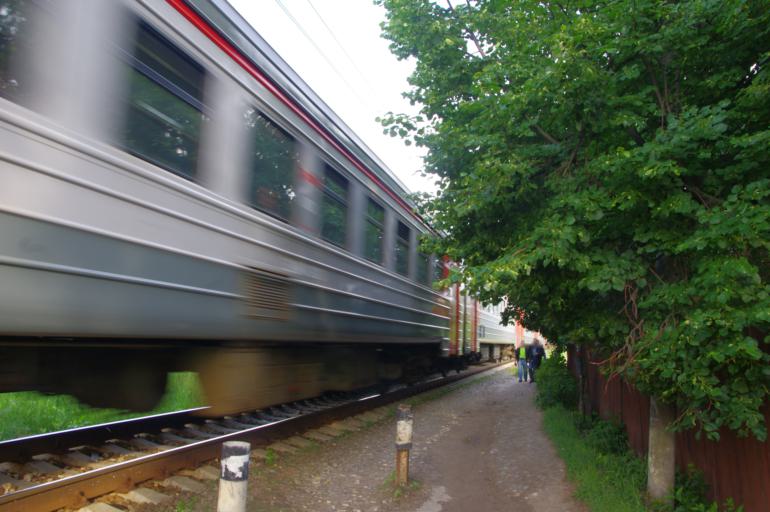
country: RU
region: Moskovskaya
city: Ramenskoye
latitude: 55.5583
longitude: 38.2440
